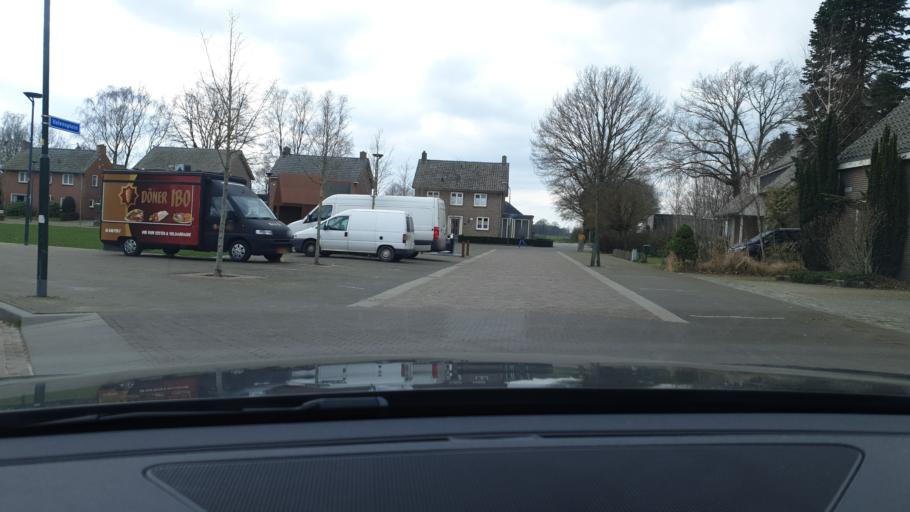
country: NL
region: North Brabant
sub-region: Gemeente Bladel en Netersel
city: Bladel
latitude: 51.3956
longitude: 5.2670
